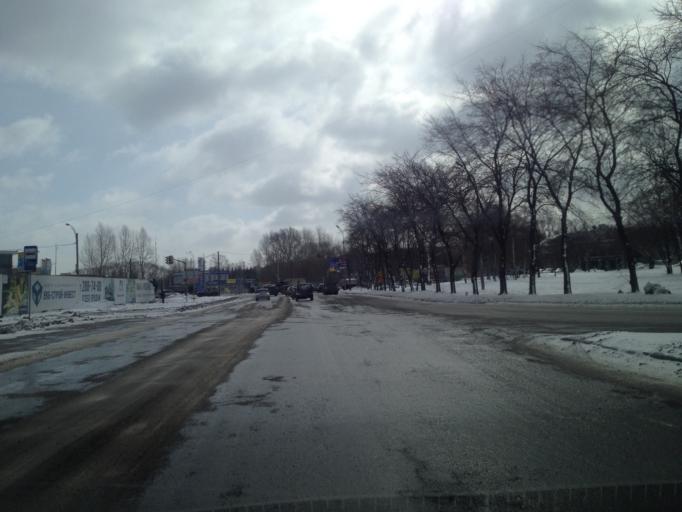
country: RU
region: Sverdlovsk
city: Yekaterinburg
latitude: 56.7990
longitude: 60.5934
